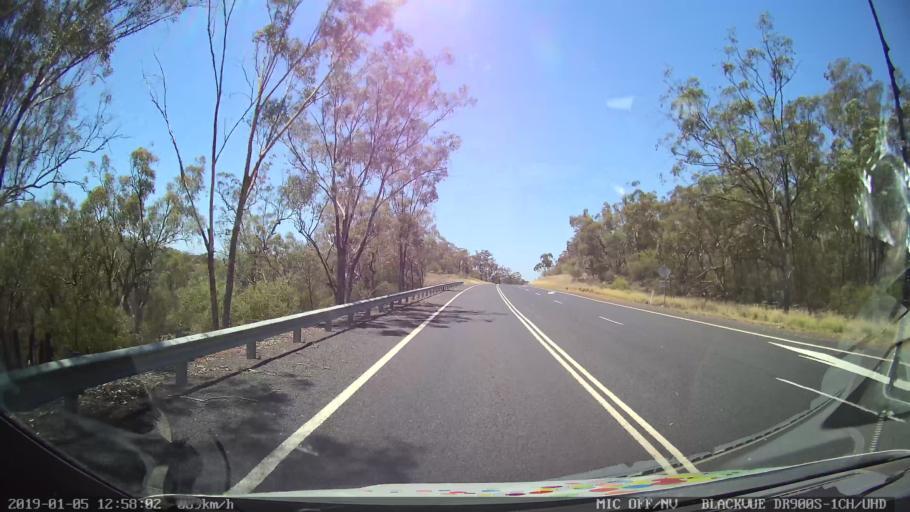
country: AU
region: New South Wales
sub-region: Warrumbungle Shire
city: Coonabarabran
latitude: -31.1100
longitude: 149.7439
